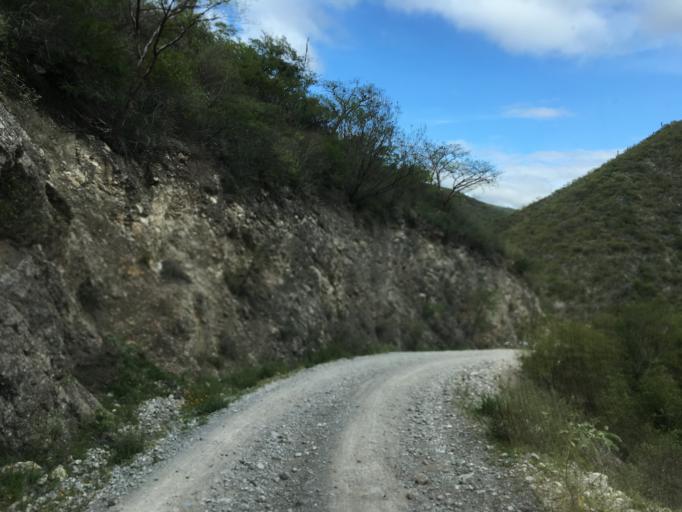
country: MX
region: Hidalgo
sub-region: Metztitlan
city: Fontezuelas
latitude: 20.6287
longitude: -98.8916
